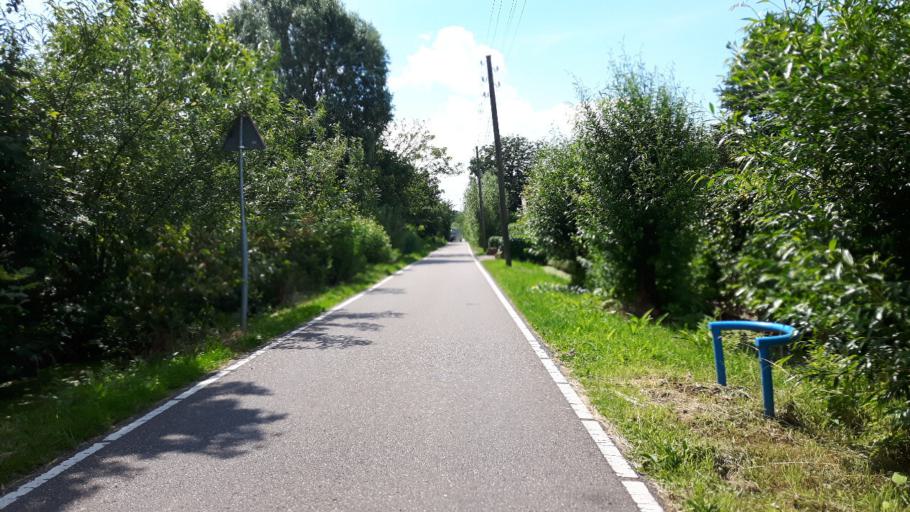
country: NL
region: South Holland
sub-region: Bodegraven-Reeuwijk
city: Reeuwijk
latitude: 52.0282
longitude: 4.7386
